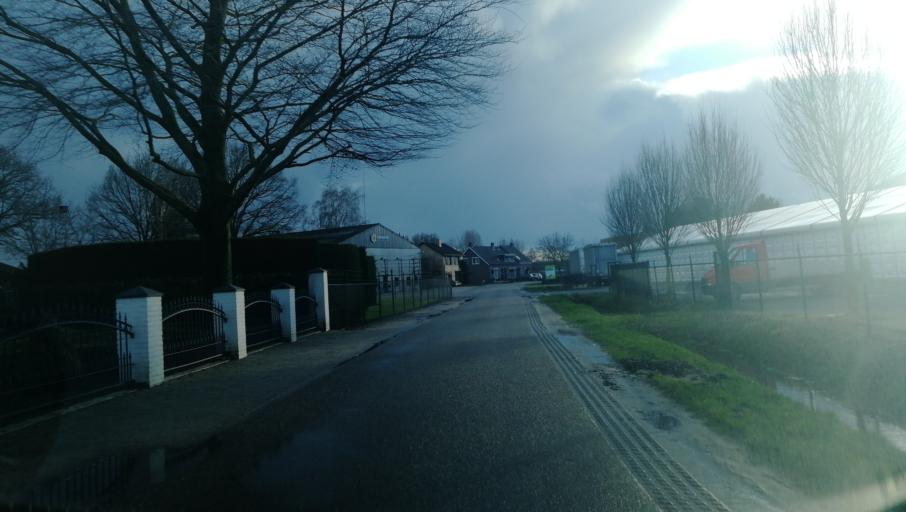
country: NL
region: Limburg
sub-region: Gemeente Peel en Maas
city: Maasbree
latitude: 51.3514
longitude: 6.0455
